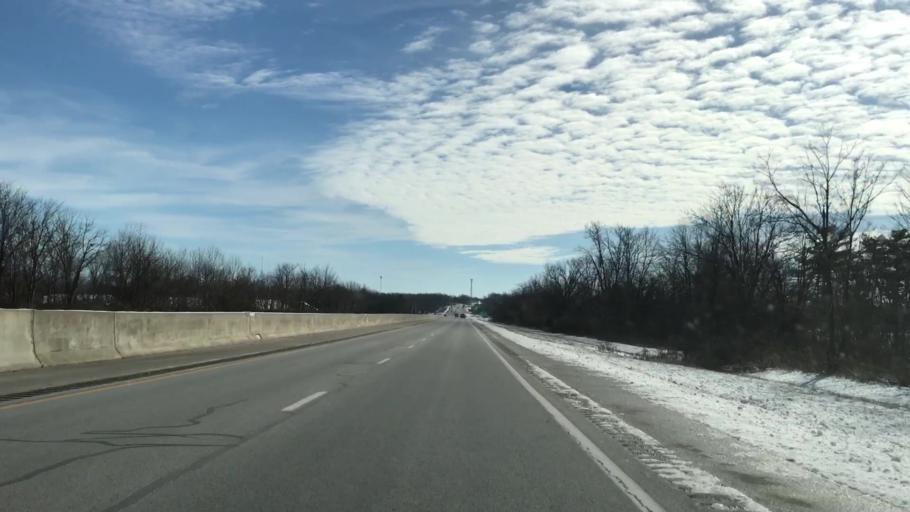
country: US
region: Kentucky
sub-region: Hardin County
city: Elizabethtown
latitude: 37.6956
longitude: -85.8778
